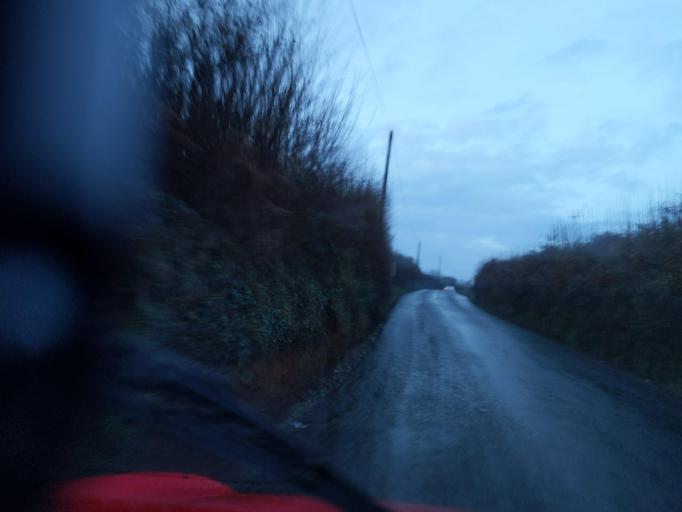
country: GB
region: England
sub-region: Devon
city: Wembury
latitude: 50.3427
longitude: -4.0752
